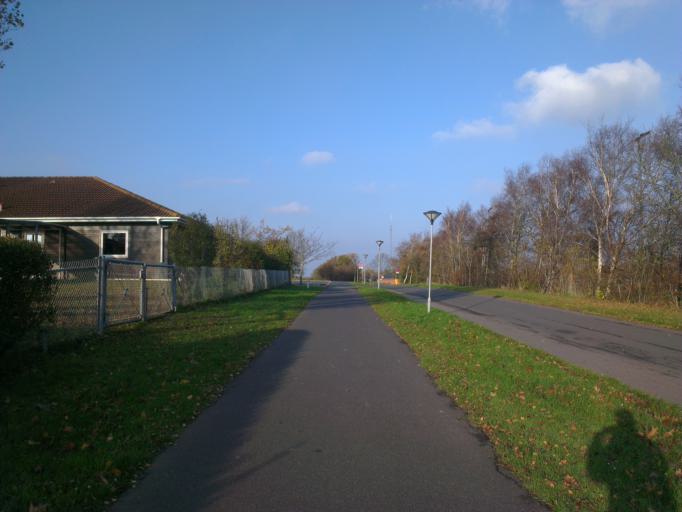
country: DK
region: Capital Region
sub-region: Frederikssund Kommune
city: Jaegerspris
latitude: 55.8430
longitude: 11.9855
